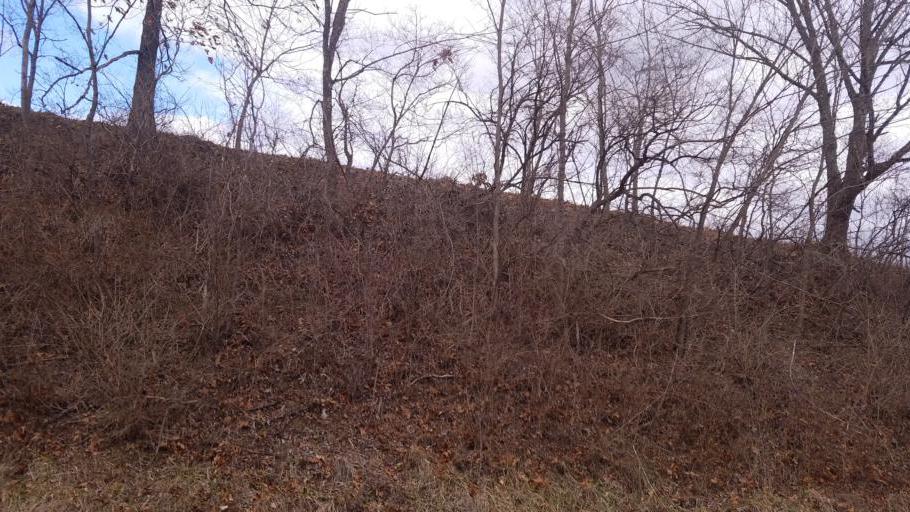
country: US
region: Ohio
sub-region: Muskingum County
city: Frazeysburg
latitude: 40.0939
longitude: -82.1970
